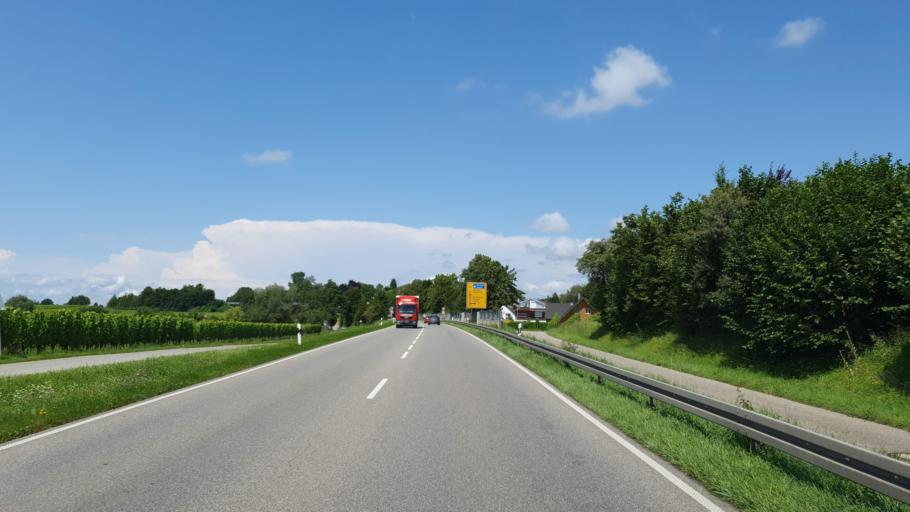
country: DE
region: Baden-Wuerttemberg
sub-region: Tuebingen Region
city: Stetten
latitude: 47.6866
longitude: 9.3016
